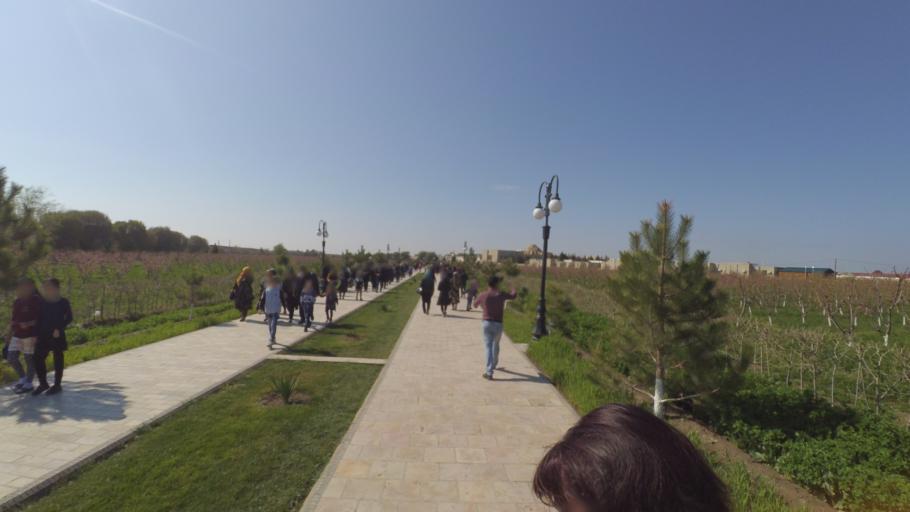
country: UZ
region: Bukhara
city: Kogon
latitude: 39.8043
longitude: 64.5398
